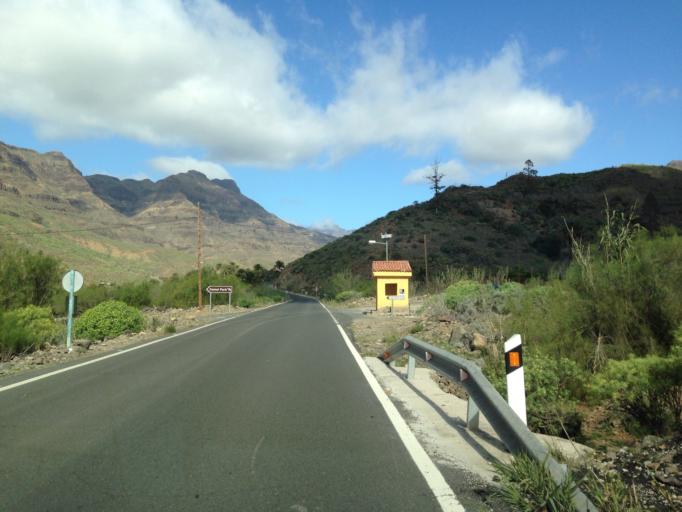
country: ES
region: Canary Islands
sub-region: Provincia de Las Palmas
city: Santa Lucia
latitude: 27.8510
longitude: -15.5651
